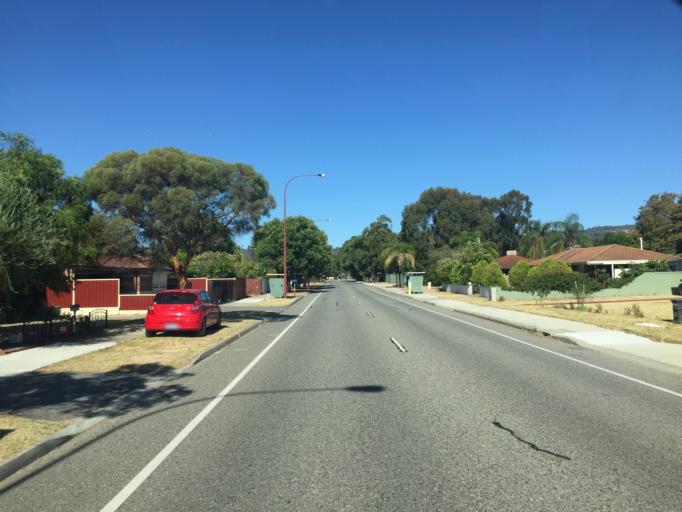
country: AU
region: Western Australia
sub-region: Gosnells
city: Gosnells
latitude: -32.0628
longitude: 116.0031
